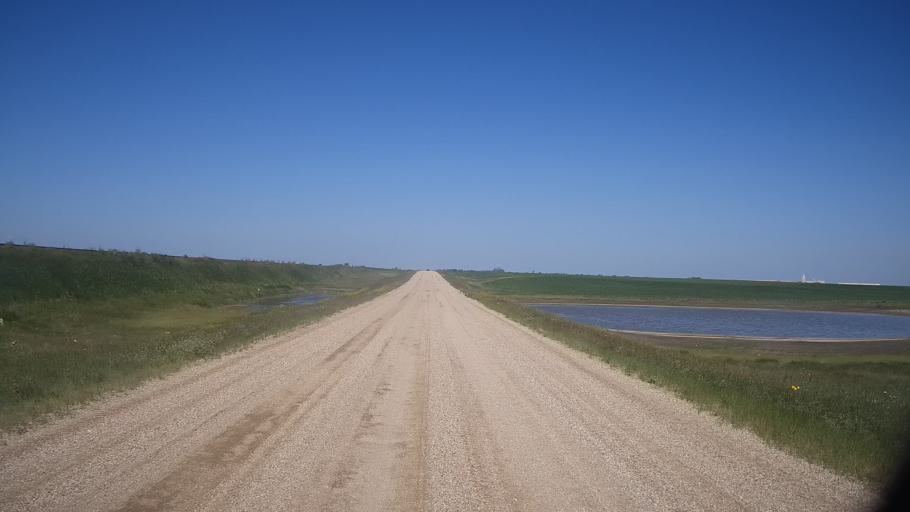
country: CA
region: Saskatchewan
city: Watrous
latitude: 51.8776
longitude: -106.0127
